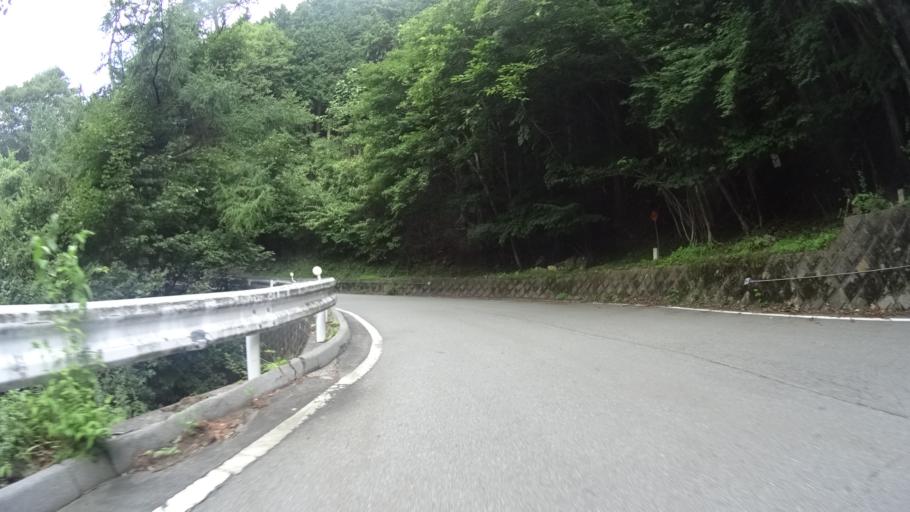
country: JP
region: Yamanashi
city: Enzan
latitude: 35.7924
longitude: 138.6871
